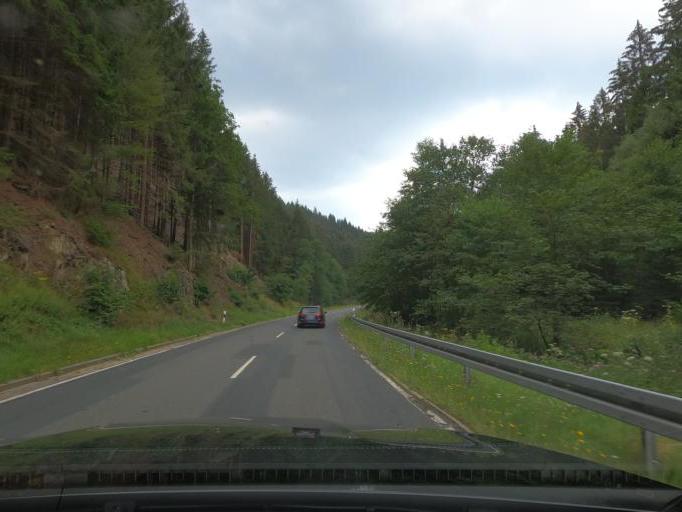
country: DE
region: Lower Saxony
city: Wildemann
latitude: 51.8446
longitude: 10.2680
